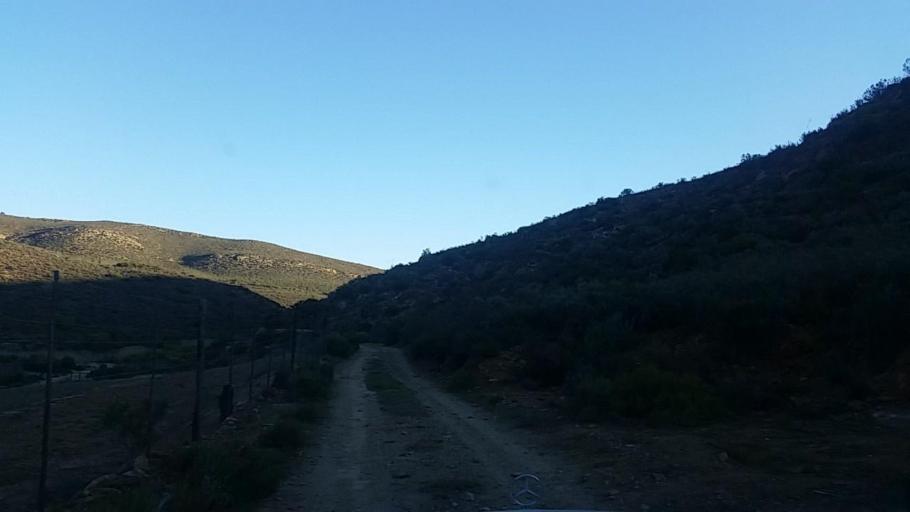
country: ZA
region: Western Cape
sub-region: Eden District Municipality
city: Knysna
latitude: -33.6577
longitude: 23.1380
